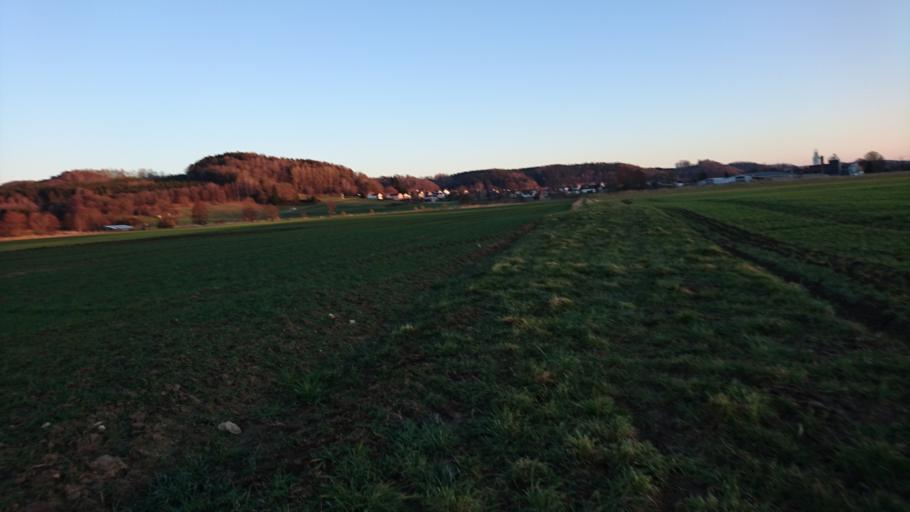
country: DE
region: Bavaria
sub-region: Swabia
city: Altenmunster
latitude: 48.4448
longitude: 10.5945
